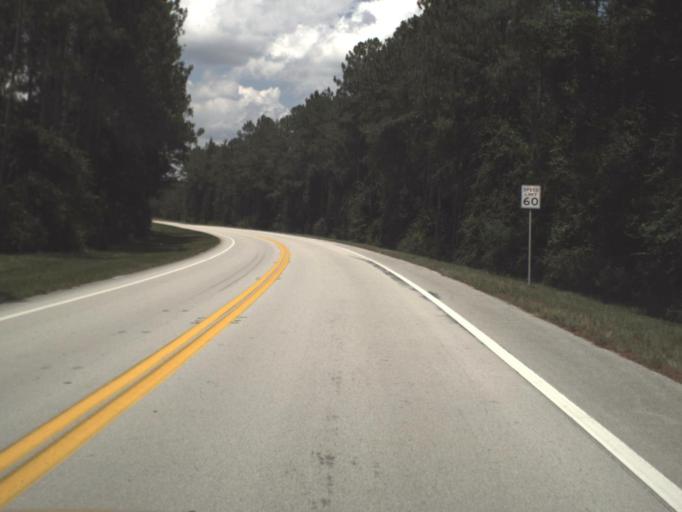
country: US
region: Florida
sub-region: Baker County
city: Macclenny
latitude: 30.1433
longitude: -82.1863
